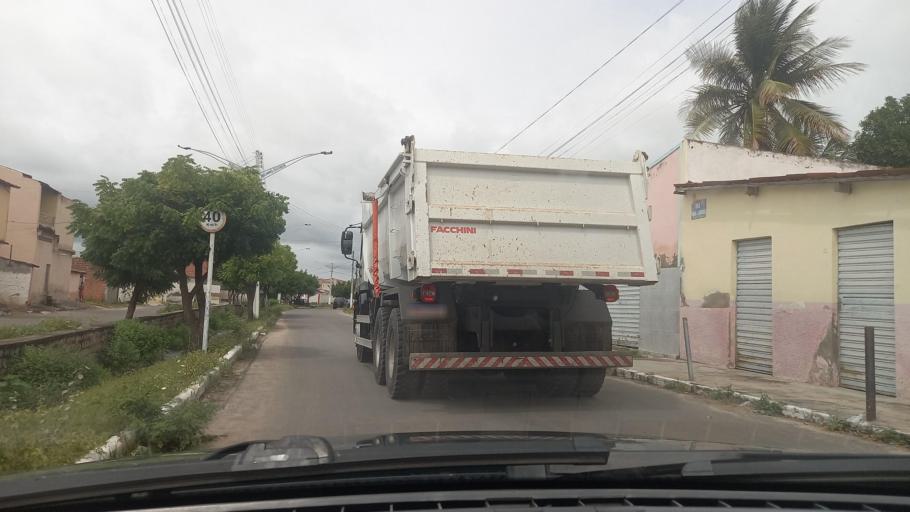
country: BR
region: Alagoas
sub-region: Delmiro Gouveia
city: Delmiro Gouveia
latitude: -9.3835
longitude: -38.0033
